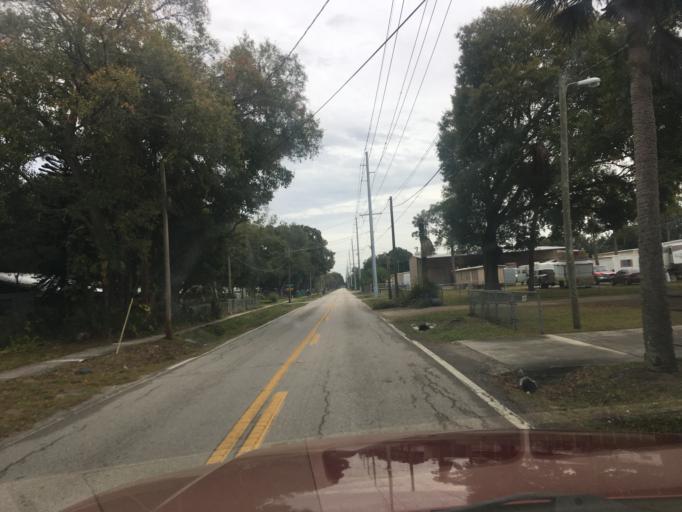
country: US
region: Florida
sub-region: Hillsborough County
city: Gibsonton
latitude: 27.8461
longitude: -82.3798
